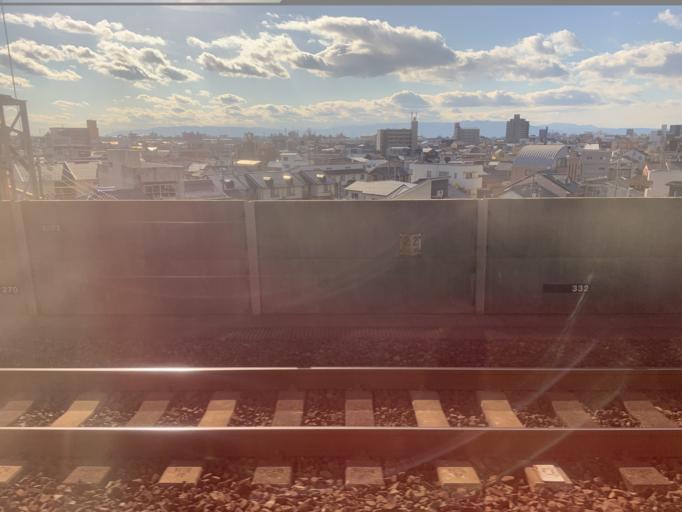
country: JP
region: Gifu
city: Gifu-shi
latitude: 35.4072
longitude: 136.7684
